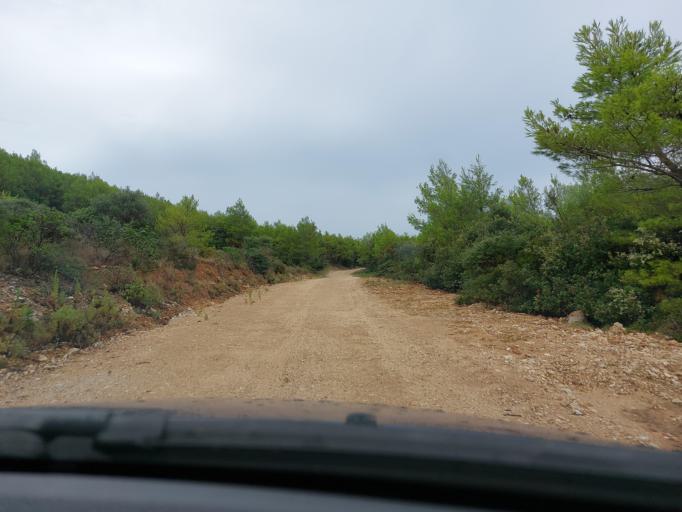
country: HR
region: Dubrovacko-Neretvanska
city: Smokvica
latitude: 42.7460
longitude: 16.9164
